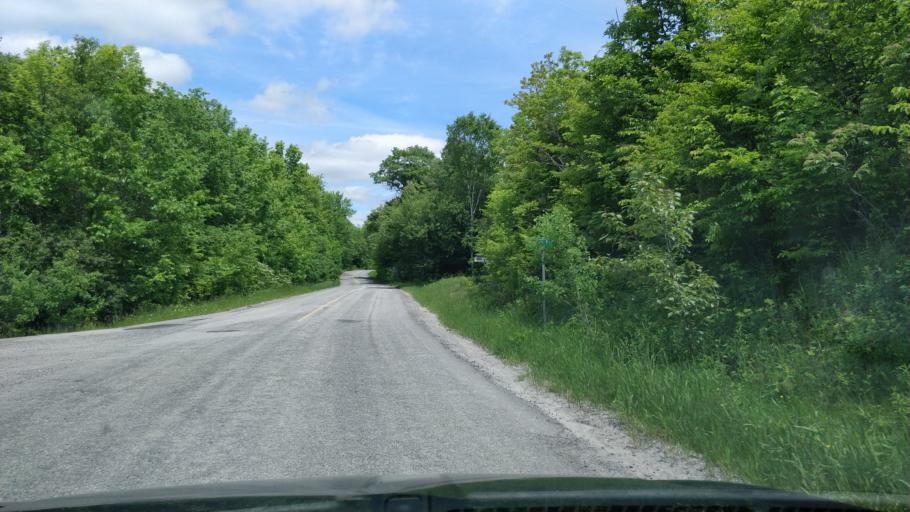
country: CA
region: Ontario
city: Perth
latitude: 44.7323
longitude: -76.5063
